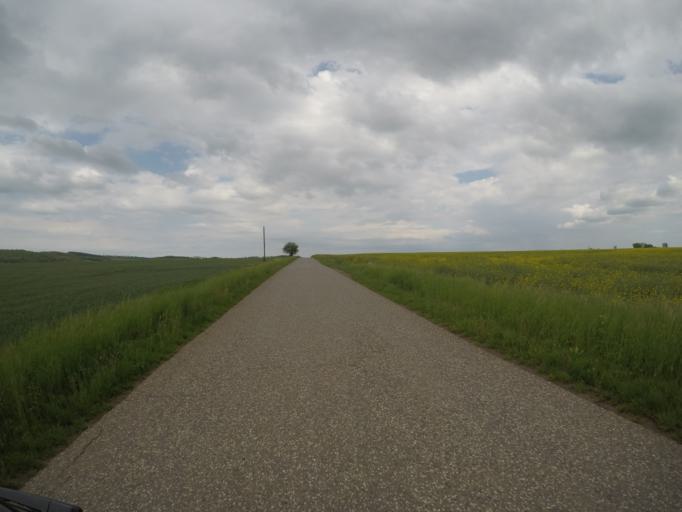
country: SK
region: Nitriansky
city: Sahy
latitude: 48.0674
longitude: 18.8583
